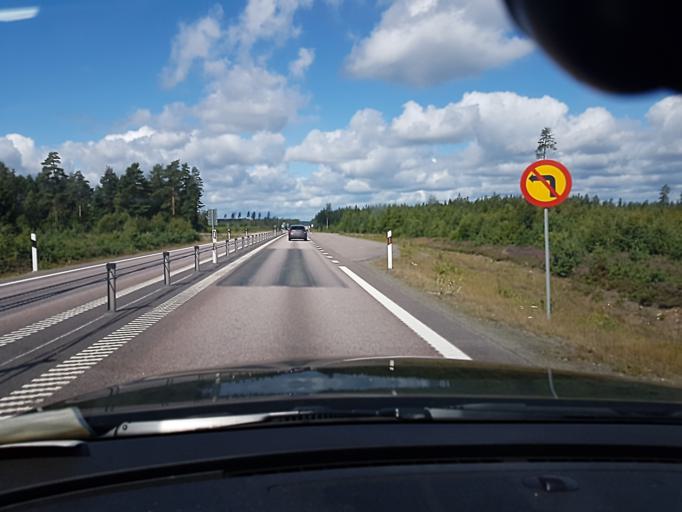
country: SE
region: Kalmar
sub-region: Emmaboda Kommun
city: Emmaboda
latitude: 56.7272
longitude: 15.5639
